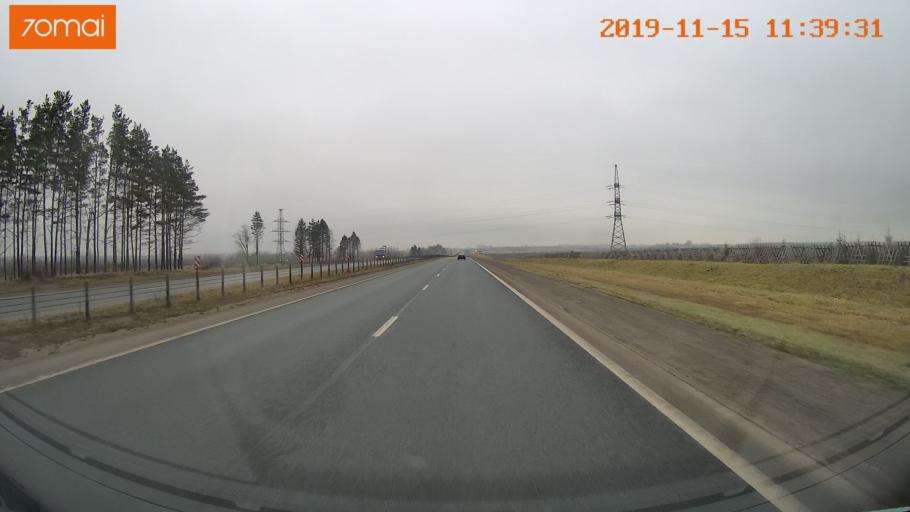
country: RU
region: Vologda
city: Molochnoye
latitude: 59.2115
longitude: 39.7267
